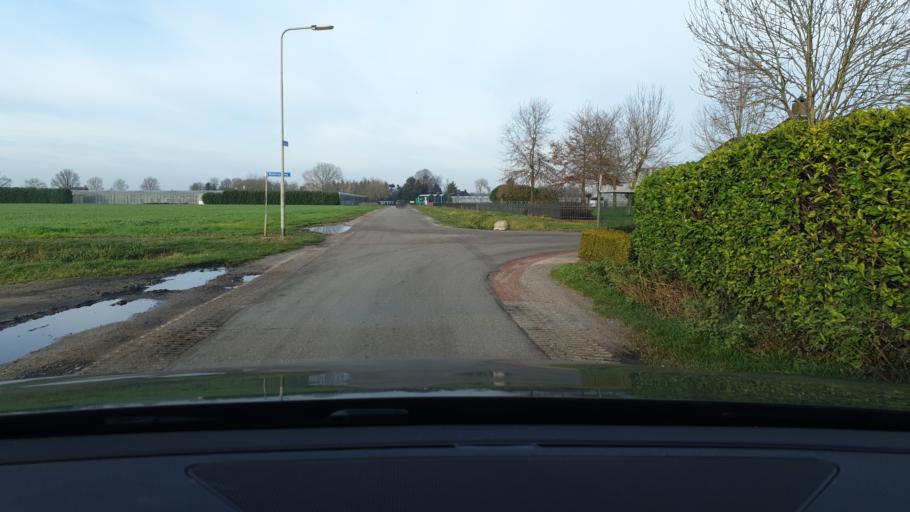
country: NL
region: Limburg
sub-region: Gemeente Venray
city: Venray
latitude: 51.4631
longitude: 6.0380
